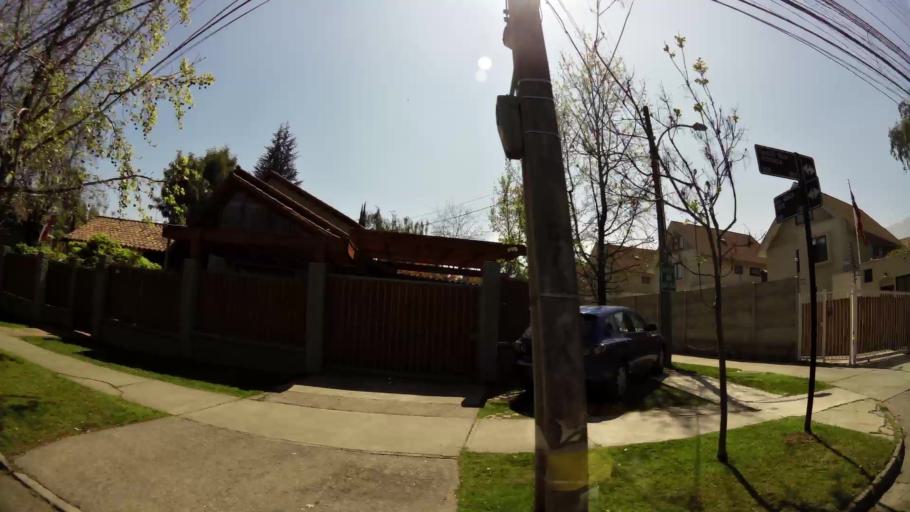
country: CL
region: Santiago Metropolitan
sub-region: Provincia de Santiago
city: Villa Presidente Frei, Nunoa, Santiago, Chile
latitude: -33.4414
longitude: -70.5302
